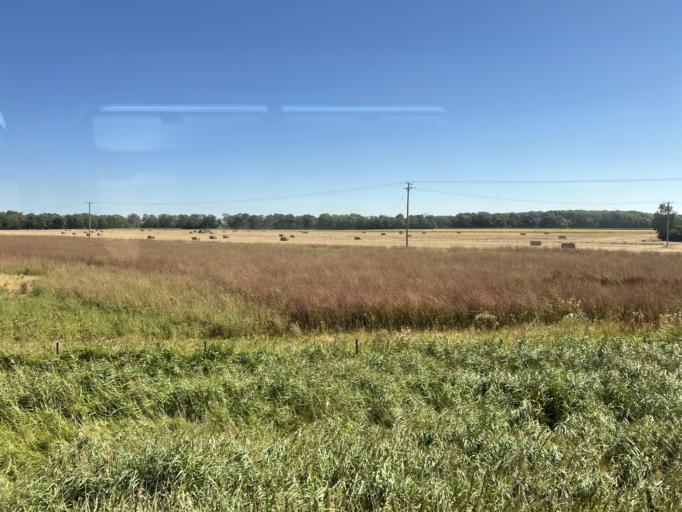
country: GB
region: England
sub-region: Lincolnshire
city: Spilsby
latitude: 53.1120
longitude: 0.1257
